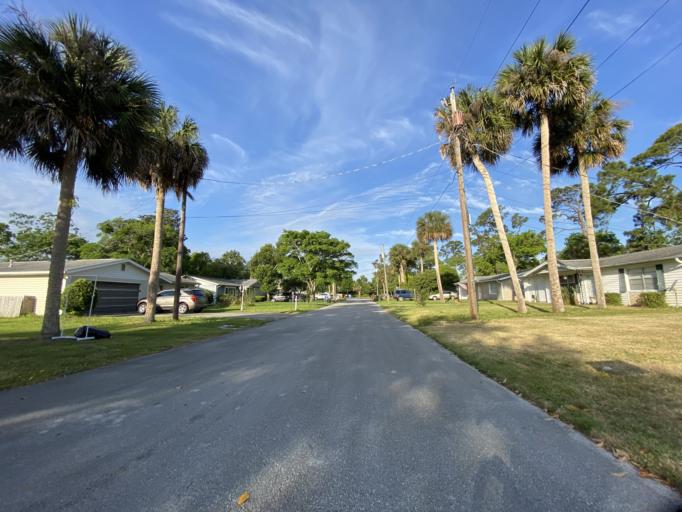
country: US
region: Florida
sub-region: Volusia County
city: South Daytona
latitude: 29.1759
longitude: -81.0096
